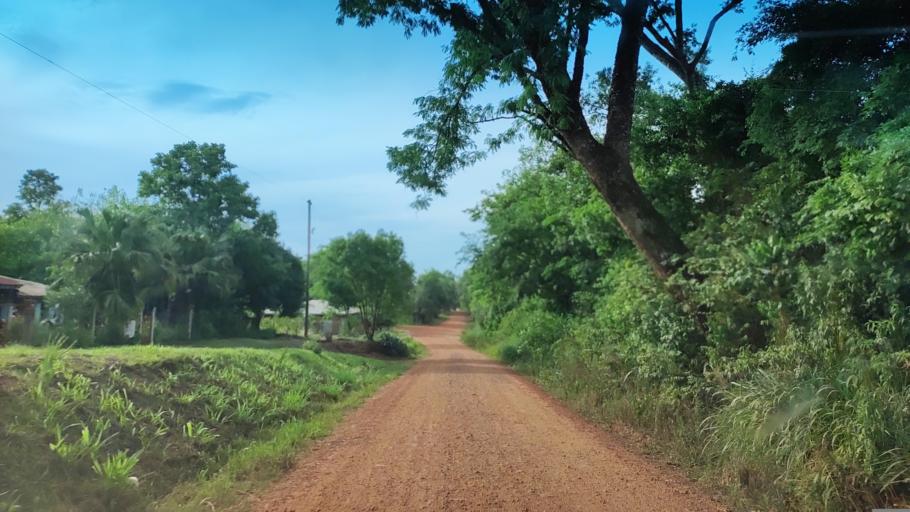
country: AR
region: Misiones
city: Gobernador Roca
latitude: -27.1501
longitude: -55.5317
